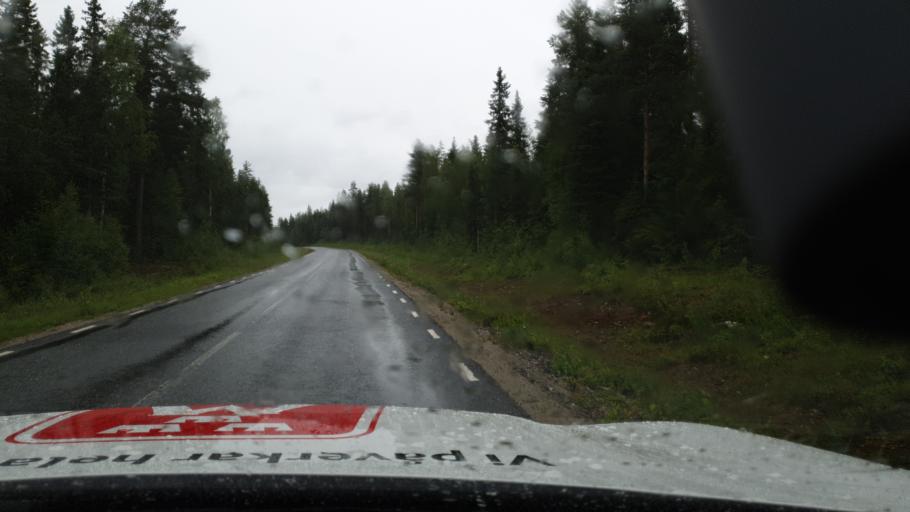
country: SE
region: Vaesterbotten
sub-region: Vindelns Kommun
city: Vindeln
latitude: 64.4753
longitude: 19.7638
